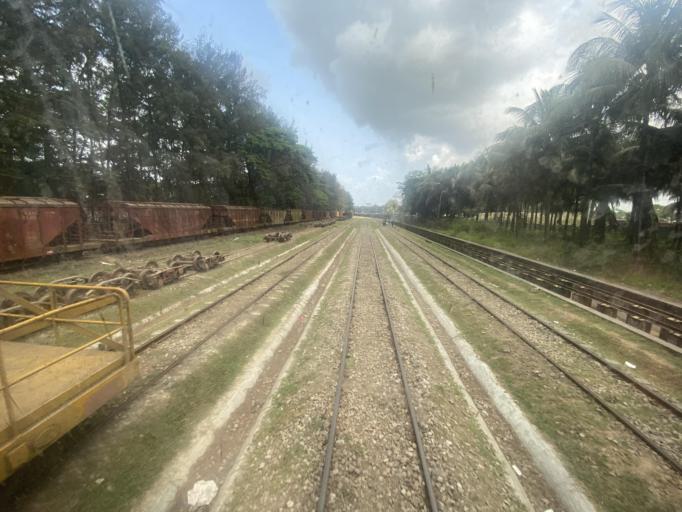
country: BD
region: Chittagong
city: Chittagong
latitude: 22.3237
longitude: 91.7802
